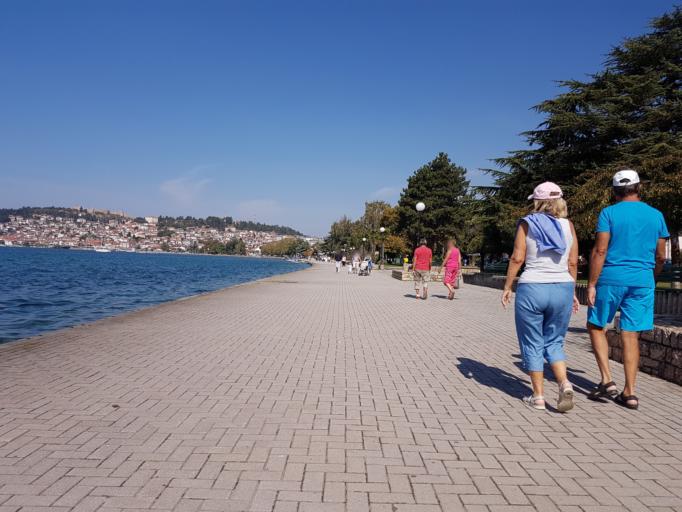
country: MK
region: Ohrid
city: Ohrid
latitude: 41.1073
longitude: 20.8067
